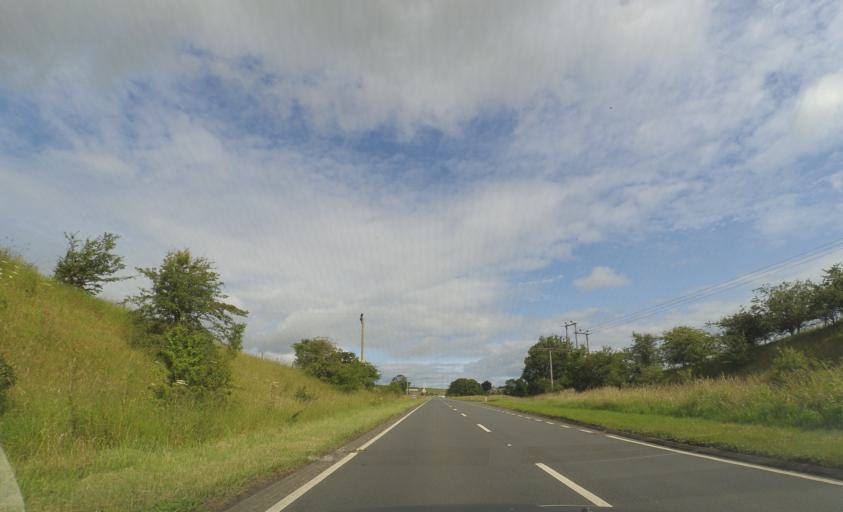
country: GB
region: Scotland
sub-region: The Scottish Borders
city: Hawick
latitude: 55.4472
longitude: -2.7757
